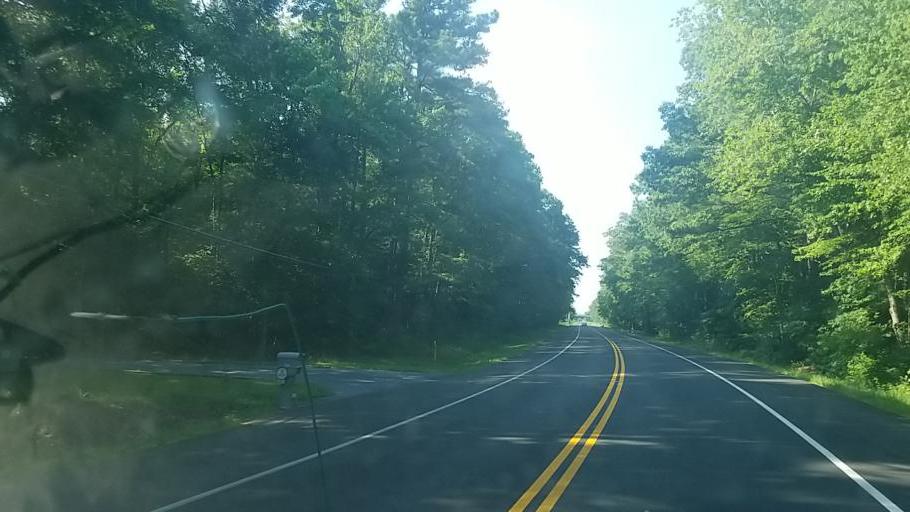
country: US
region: Maryland
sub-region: Worcester County
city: Ocean Pines
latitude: 38.3710
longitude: -75.1982
